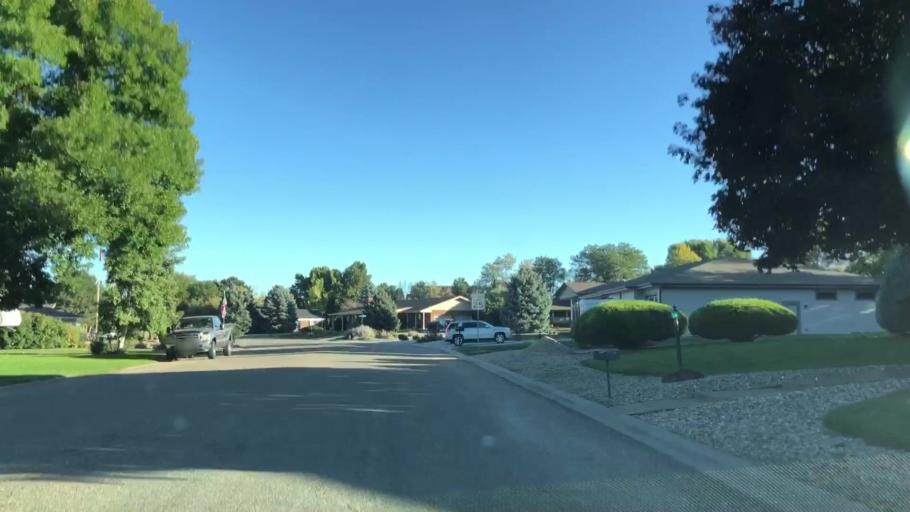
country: US
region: Colorado
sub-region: Larimer County
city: Loveland
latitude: 40.4288
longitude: -105.0221
